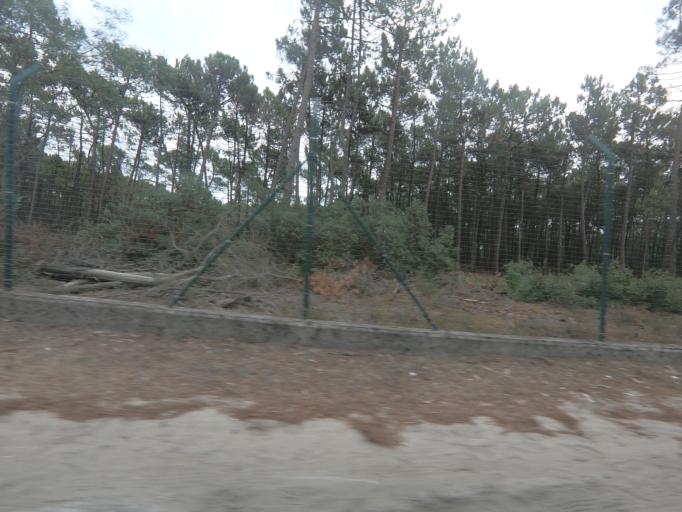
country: PT
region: Setubal
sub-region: Almada
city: Charneca
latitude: 38.5909
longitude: -9.1916
